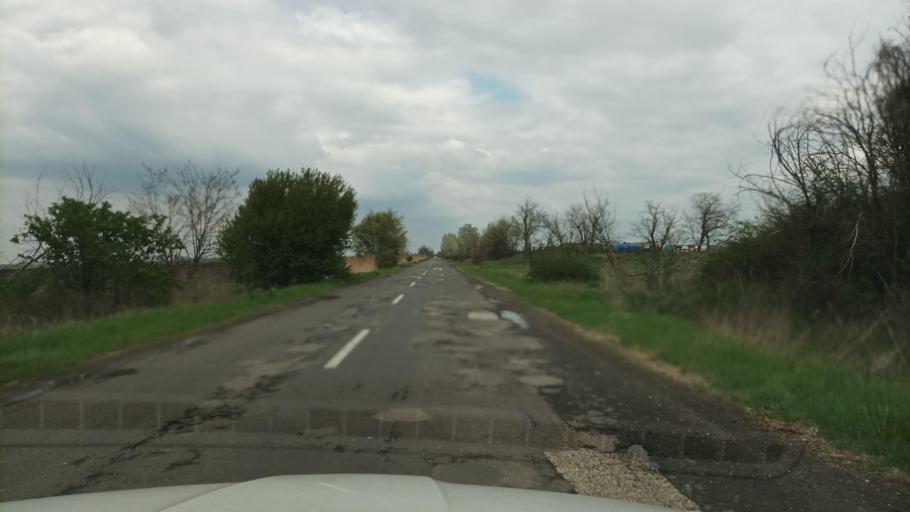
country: HU
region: Pest
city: Abony
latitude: 47.1572
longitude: 19.9699
